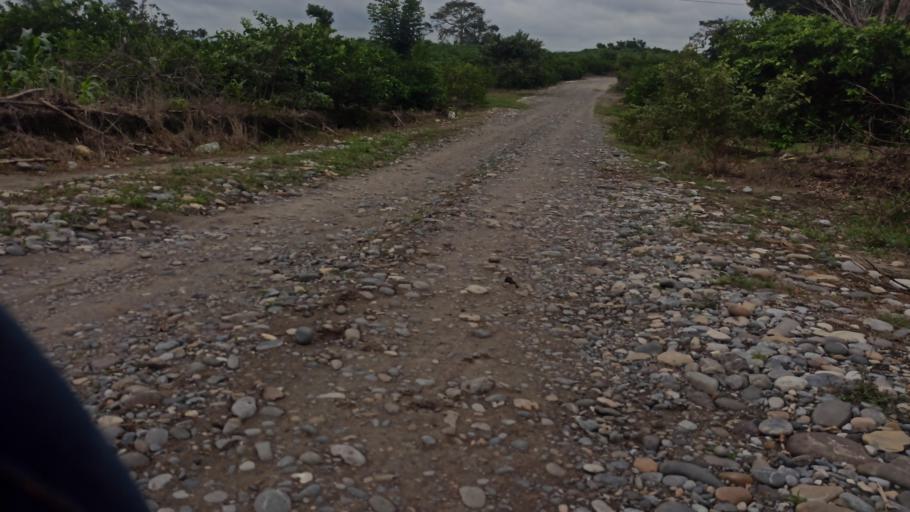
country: MX
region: Puebla
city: Espinal
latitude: 20.2928
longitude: -97.3984
